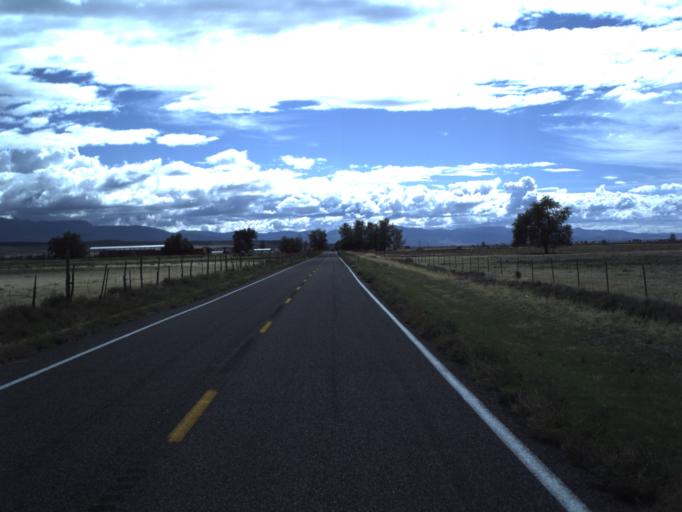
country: US
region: Utah
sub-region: Millard County
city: Fillmore
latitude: 39.0647
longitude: -112.4098
